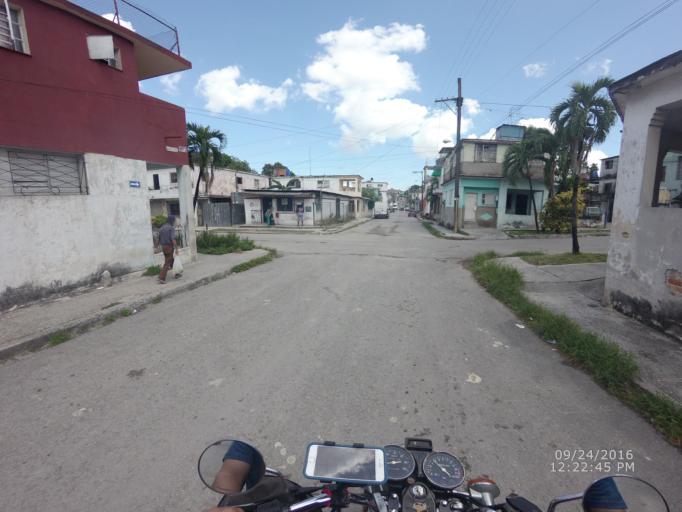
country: CU
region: La Habana
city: Diez de Octubre
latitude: 23.0974
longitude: -82.3539
